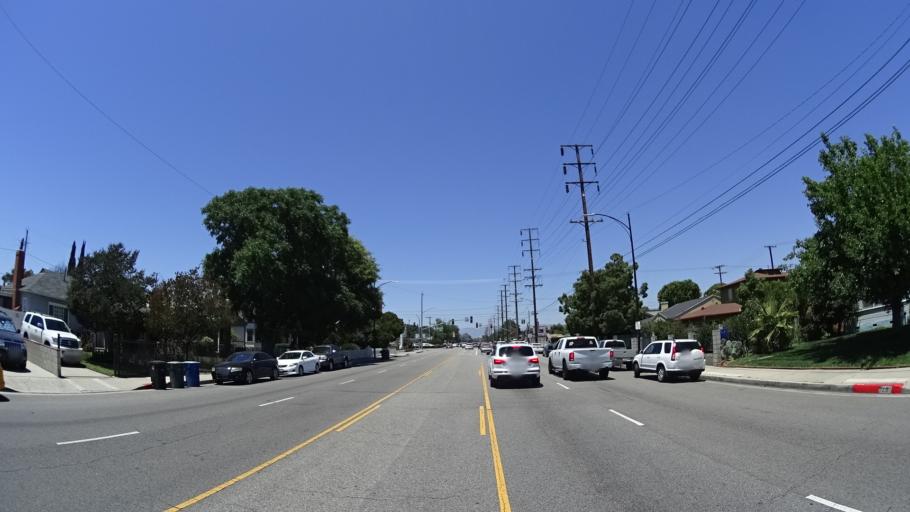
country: US
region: California
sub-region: Los Angeles County
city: Burbank
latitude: 34.1709
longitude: -118.3342
